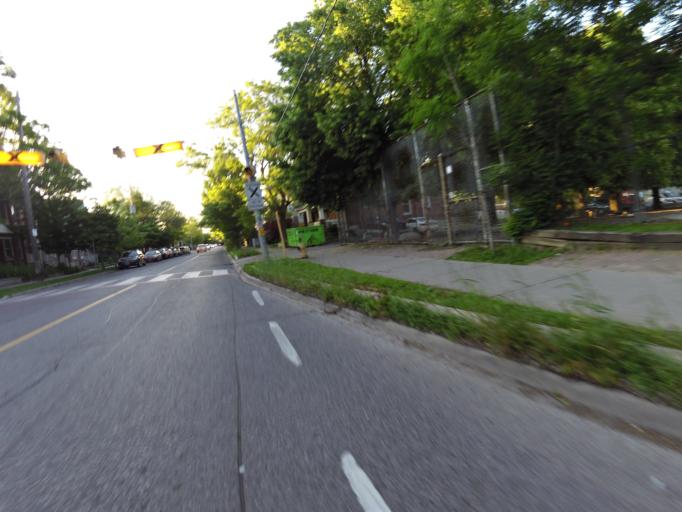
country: CA
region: Ontario
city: Toronto
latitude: 43.6440
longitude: -79.4380
